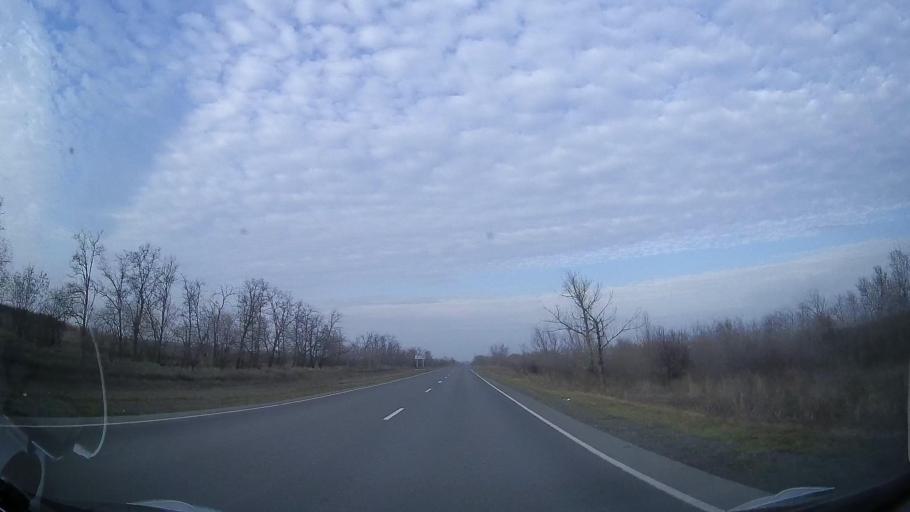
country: RU
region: Rostov
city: Bagayevskaya
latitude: 47.1545
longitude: 40.2764
